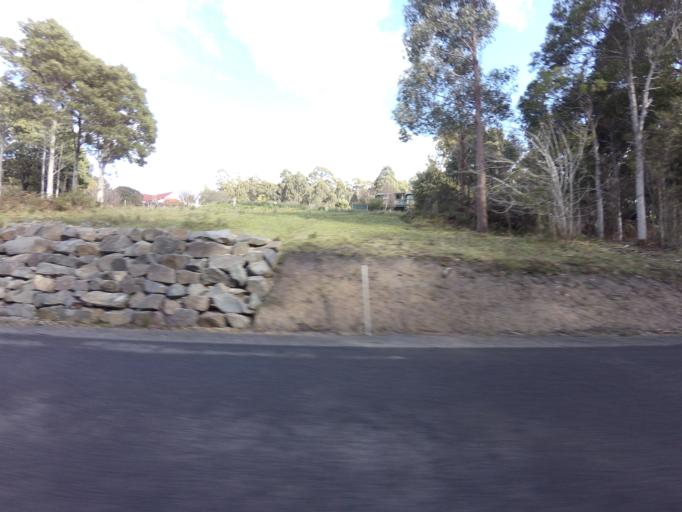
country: AU
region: Tasmania
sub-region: Huon Valley
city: Geeveston
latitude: -43.4282
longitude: 146.9058
